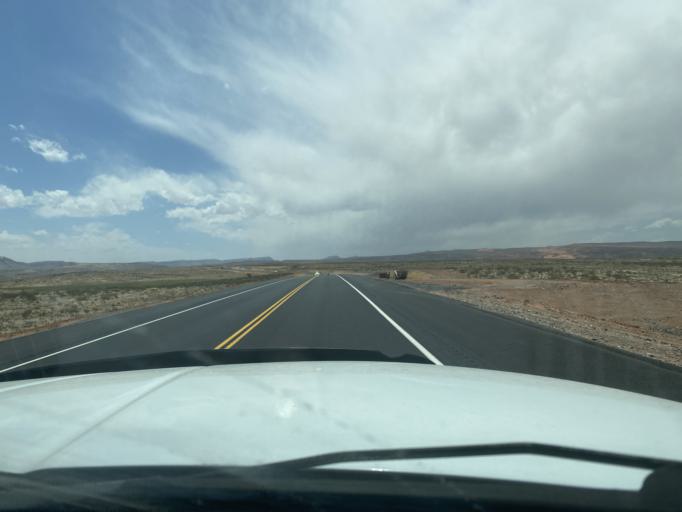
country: US
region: Utah
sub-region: Washington County
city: Hurricane
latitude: 37.1415
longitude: -113.3470
